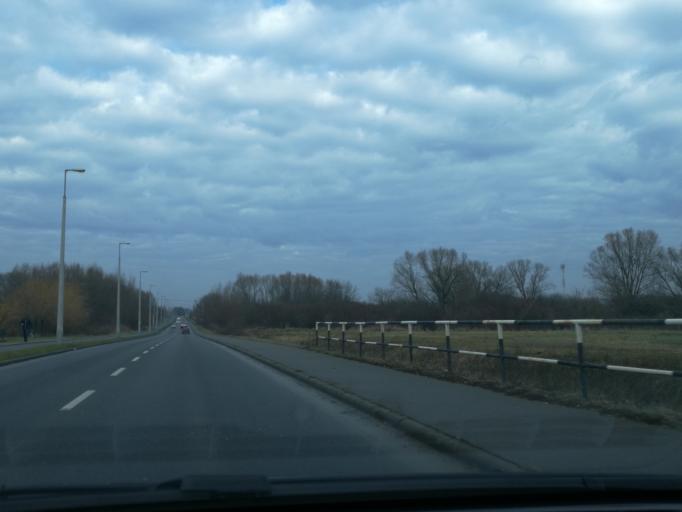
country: HU
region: Szabolcs-Szatmar-Bereg
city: Nyiregyhaza
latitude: 47.9638
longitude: 21.7434
